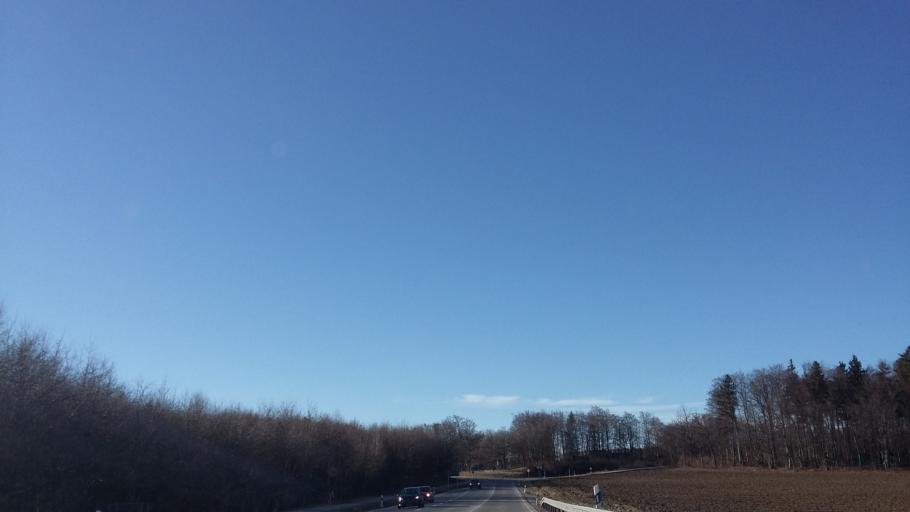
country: DE
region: Bavaria
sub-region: Upper Bavaria
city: Pocking
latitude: 47.9824
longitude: 11.3126
